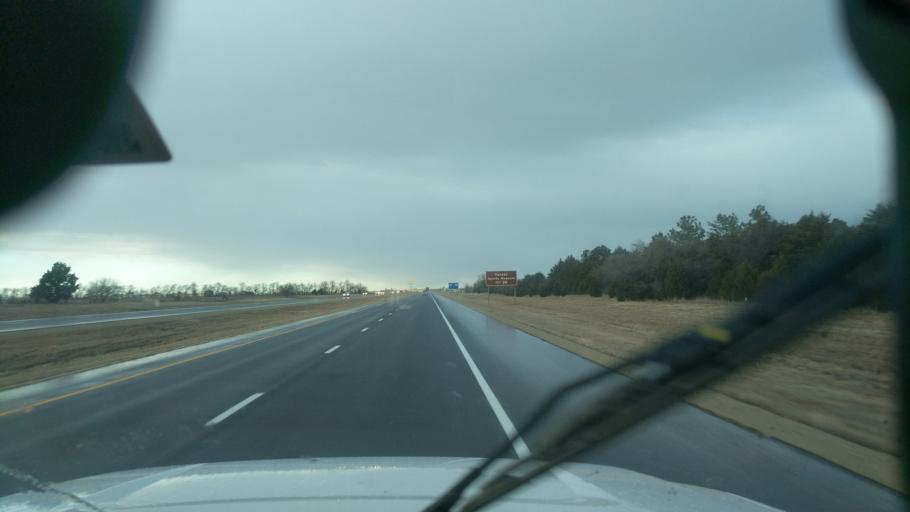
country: US
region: Kansas
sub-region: Harvey County
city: Newton
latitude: 37.9864
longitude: -97.3271
